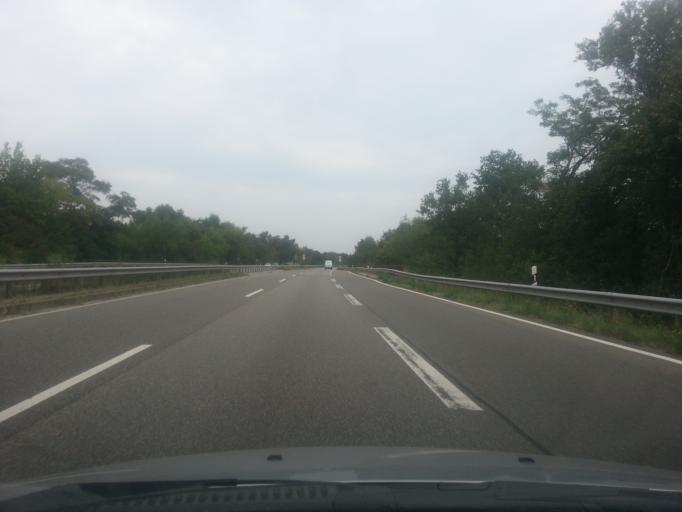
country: DE
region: Rheinland-Pfalz
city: Speyer
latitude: 49.3350
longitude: 8.4096
